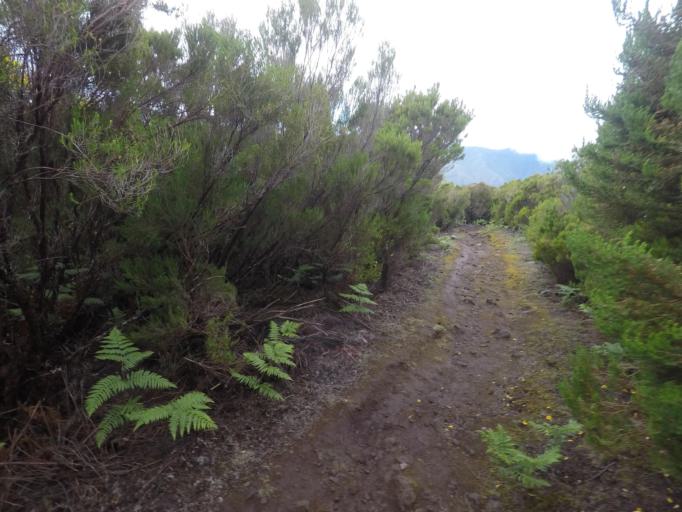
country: PT
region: Madeira
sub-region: Calheta
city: Arco da Calheta
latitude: 32.7790
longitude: -17.1328
